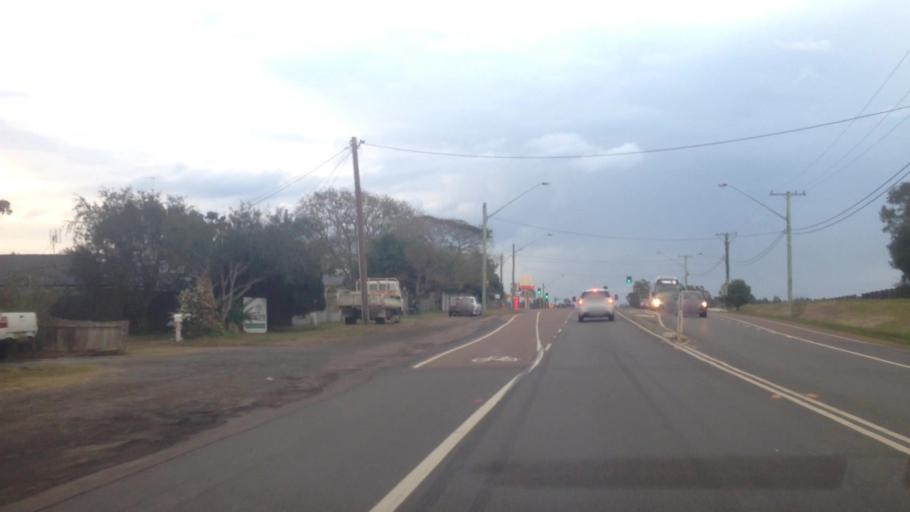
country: AU
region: New South Wales
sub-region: Wyong Shire
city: Tuggerawong
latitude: -33.2670
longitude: 151.4547
